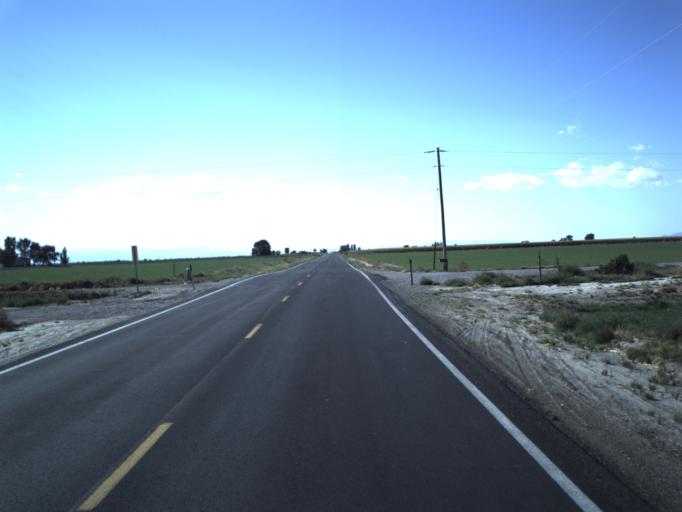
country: US
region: Utah
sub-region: Millard County
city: Delta
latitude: 39.2802
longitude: -112.6529
